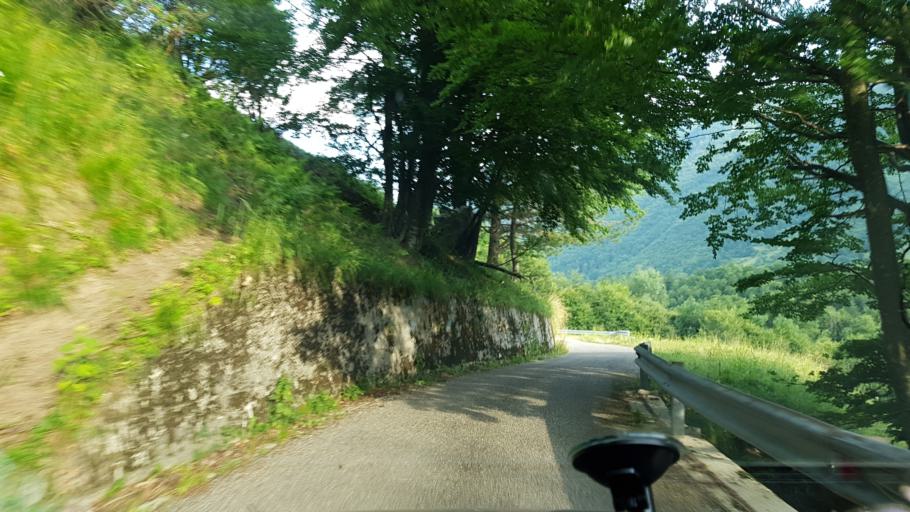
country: IT
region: Friuli Venezia Giulia
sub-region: Provincia di Udine
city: Prato
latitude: 46.3354
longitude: 13.3309
